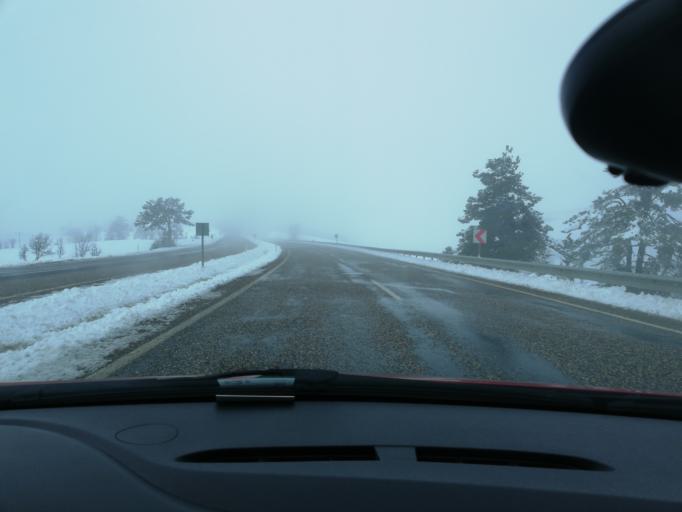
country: TR
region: Kastamonu
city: Akkaya
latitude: 41.2965
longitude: 33.4893
